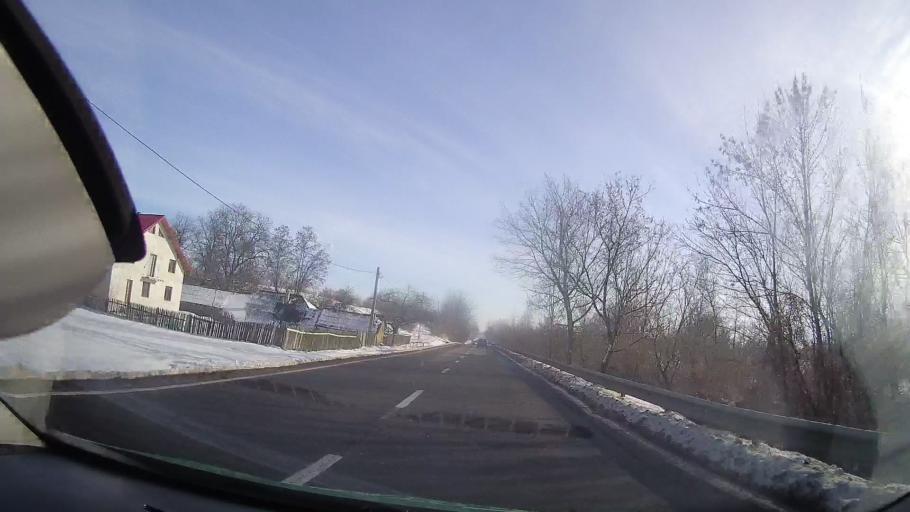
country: RO
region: Neamt
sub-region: Comuna Negresti
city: Negresti
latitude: 47.0715
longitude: 26.3633
